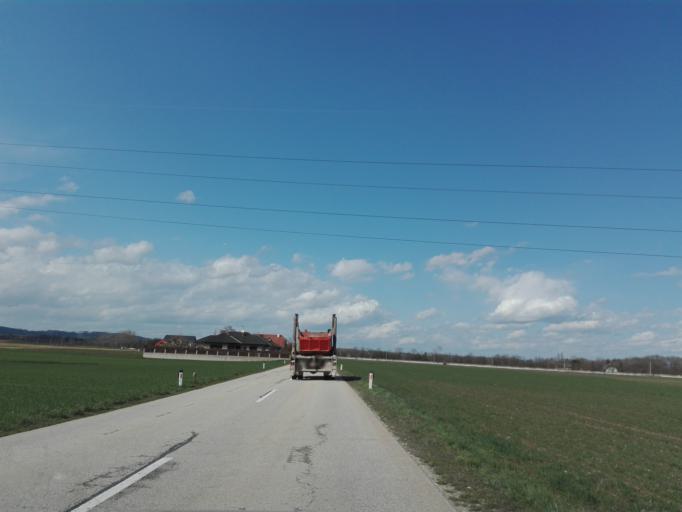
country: AT
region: Upper Austria
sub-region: Wels-Land
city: Marchtrenk
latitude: 48.2037
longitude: 14.1354
